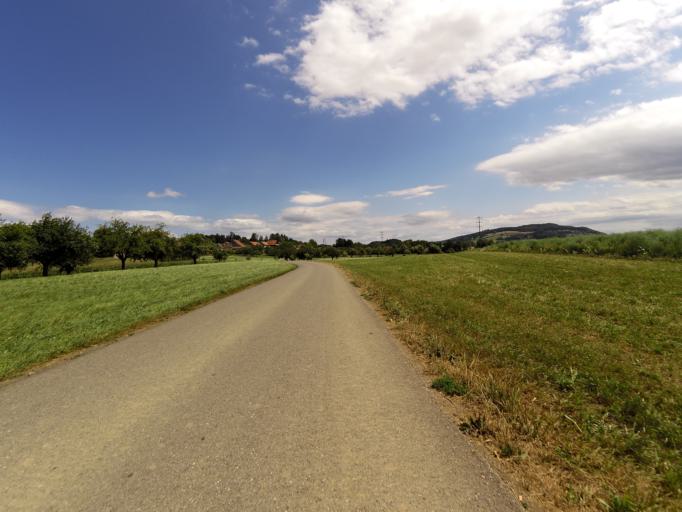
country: CH
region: Thurgau
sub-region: Weinfelden District
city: Wigoltingen
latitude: 47.5981
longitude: 9.0481
